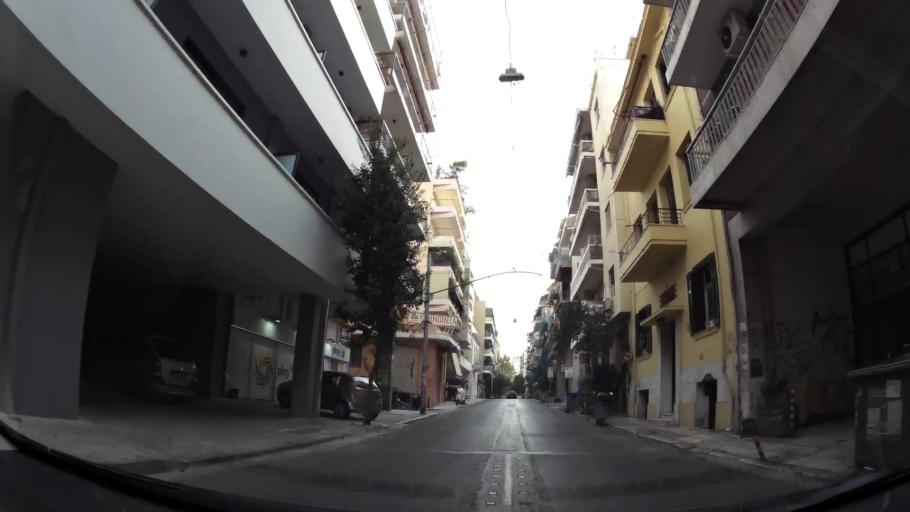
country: GR
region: Attica
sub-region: Nomarchia Athinas
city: Kipseli
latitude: 37.9880
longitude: 23.7432
